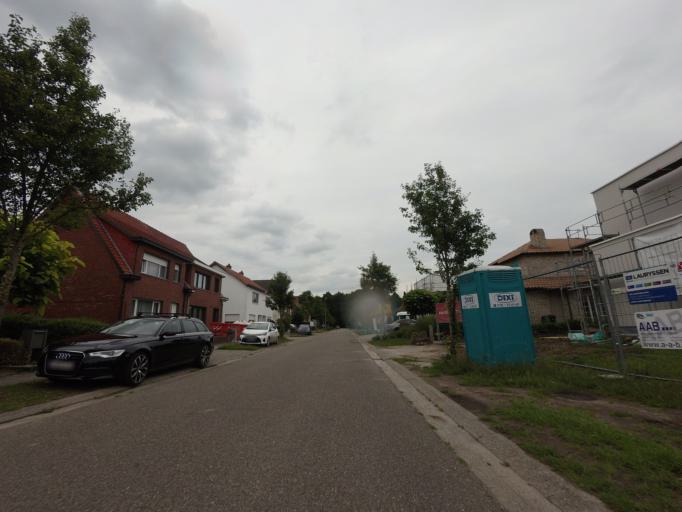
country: BE
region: Flanders
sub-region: Provincie Antwerpen
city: Schilde
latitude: 51.2389
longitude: 4.5936
